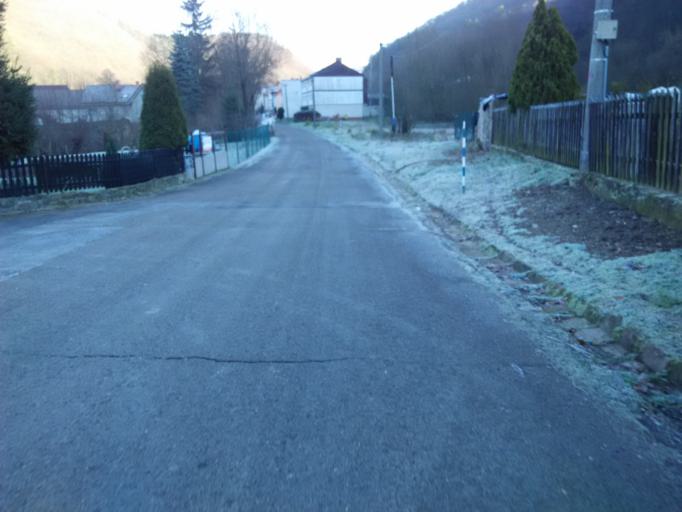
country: SK
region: Banskobystricky
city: Zarnovica
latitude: 48.5265
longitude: 18.7447
